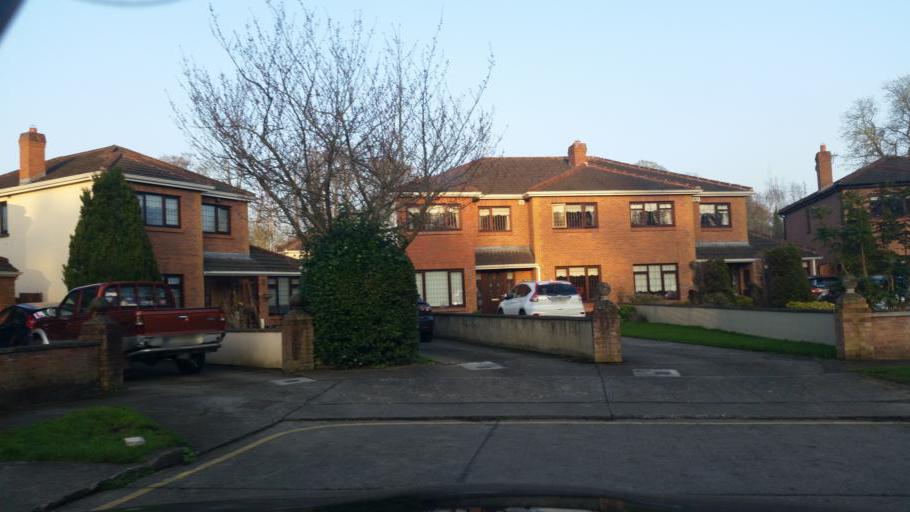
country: IE
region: Leinster
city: Hartstown
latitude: 53.3846
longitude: -6.4260
